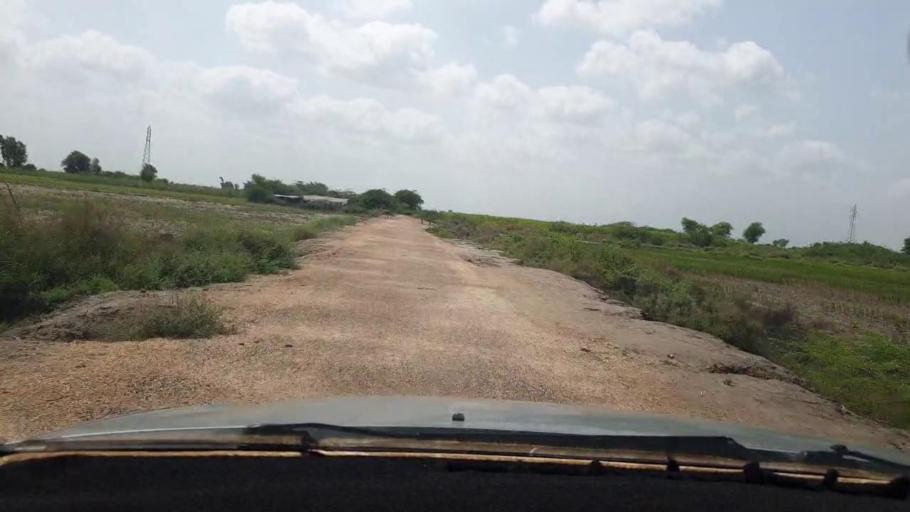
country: PK
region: Sindh
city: Tando Bago
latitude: 24.7507
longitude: 69.1532
